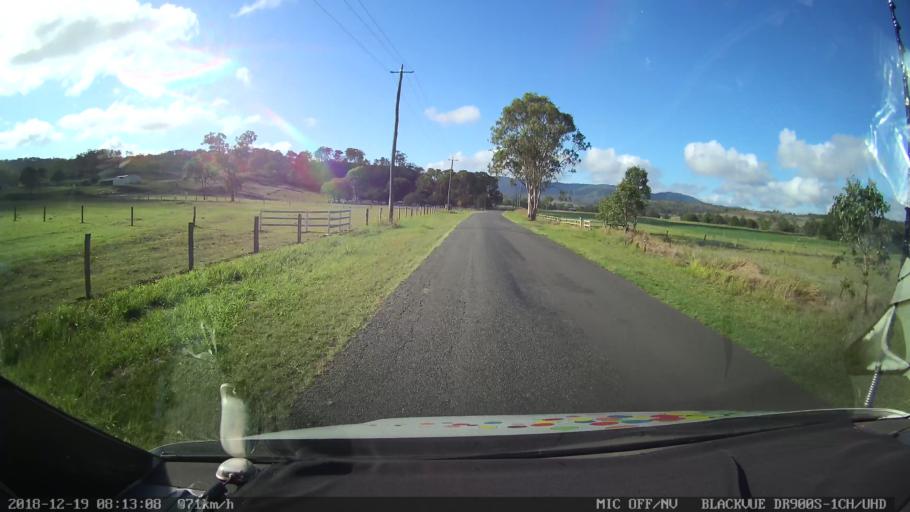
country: AU
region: Queensland
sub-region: Logan
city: Cedar Vale
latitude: -28.2354
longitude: 152.8912
